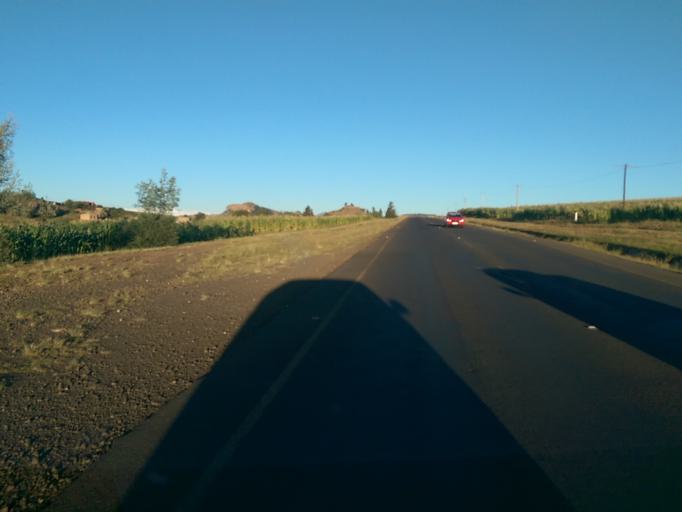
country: LS
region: Maseru
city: Maseru
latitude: -29.4082
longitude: 27.5986
